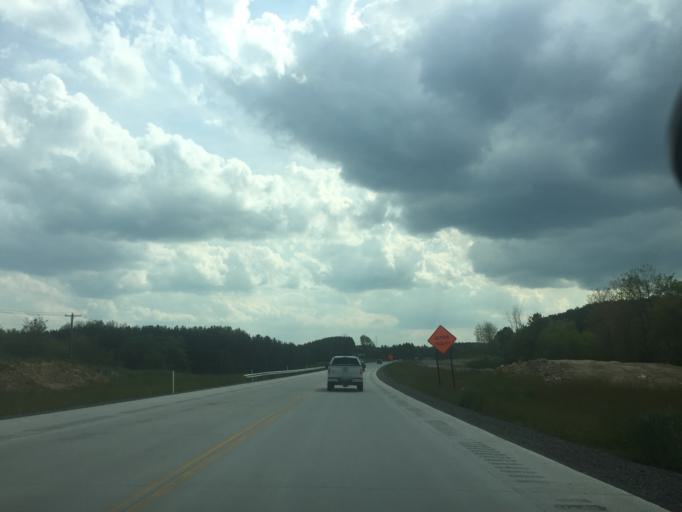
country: US
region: West Virginia
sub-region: Tucker County
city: Parsons
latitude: 39.1401
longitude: -79.4568
